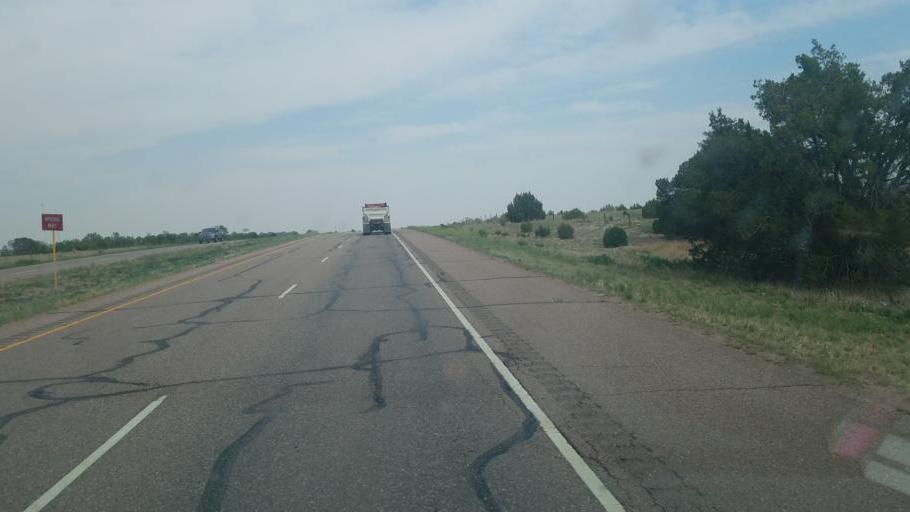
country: US
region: Colorado
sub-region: Fremont County
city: Penrose
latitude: 38.4138
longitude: -105.0238
